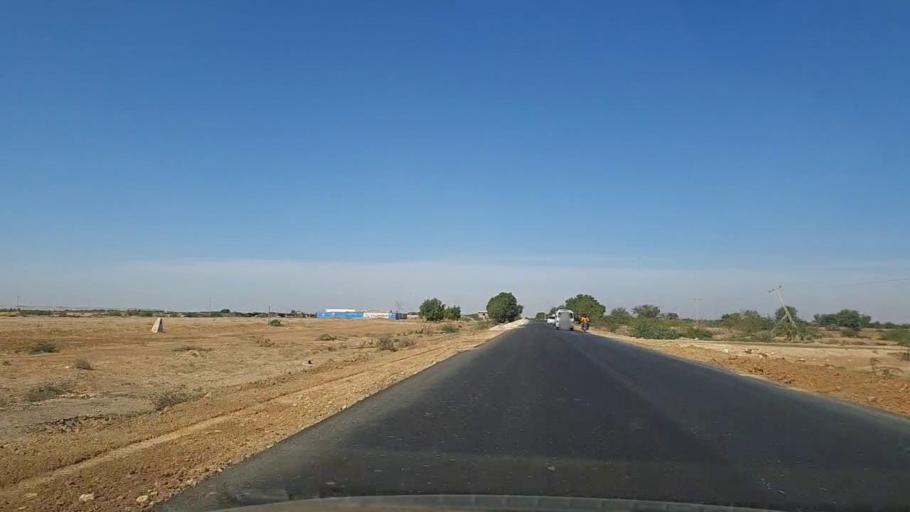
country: PK
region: Sindh
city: Kotri
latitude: 25.2490
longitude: 68.2281
